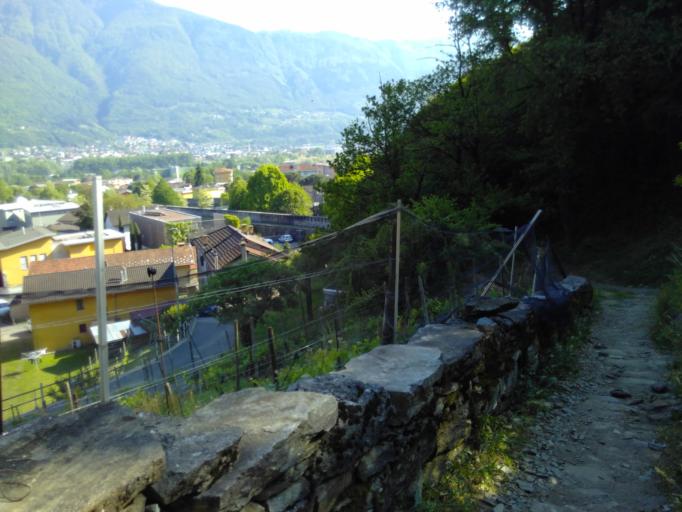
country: CH
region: Ticino
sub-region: Bellinzona District
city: Sementina
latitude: 46.1881
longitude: 8.9923
